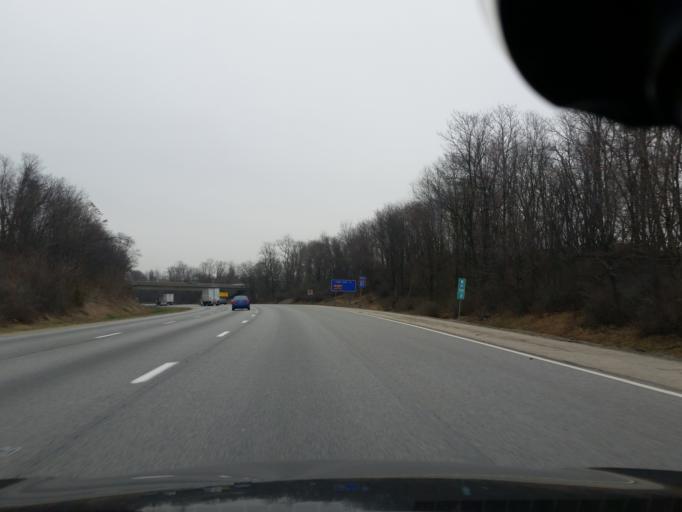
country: US
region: Pennsylvania
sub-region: Cumberland County
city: Enola
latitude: 40.2757
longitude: -76.9901
